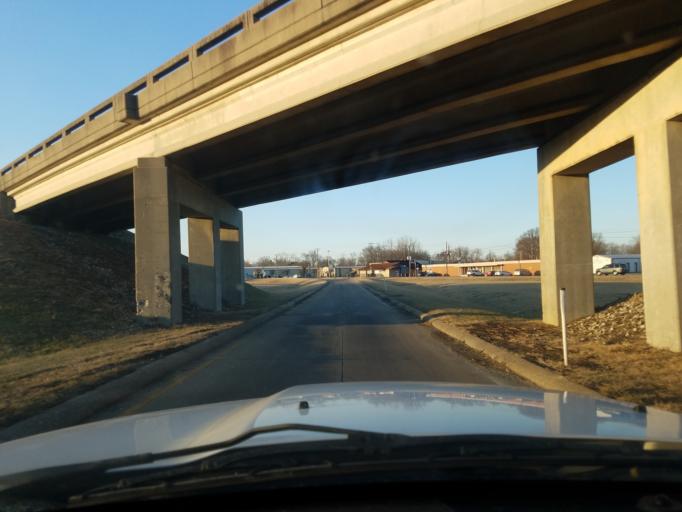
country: US
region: Kentucky
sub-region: Henderson County
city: Henderson
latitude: 37.8248
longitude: -87.5672
